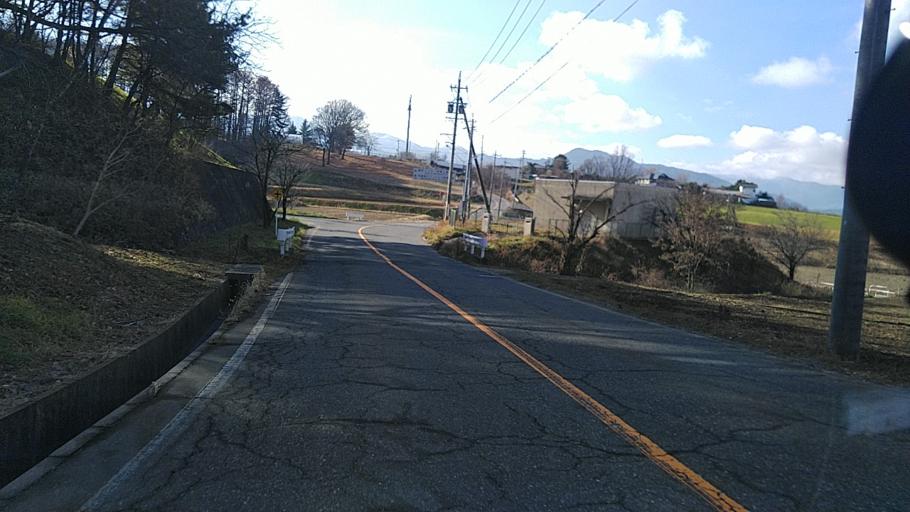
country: JP
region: Nagano
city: Shiojiri
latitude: 36.1258
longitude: 137.9815
